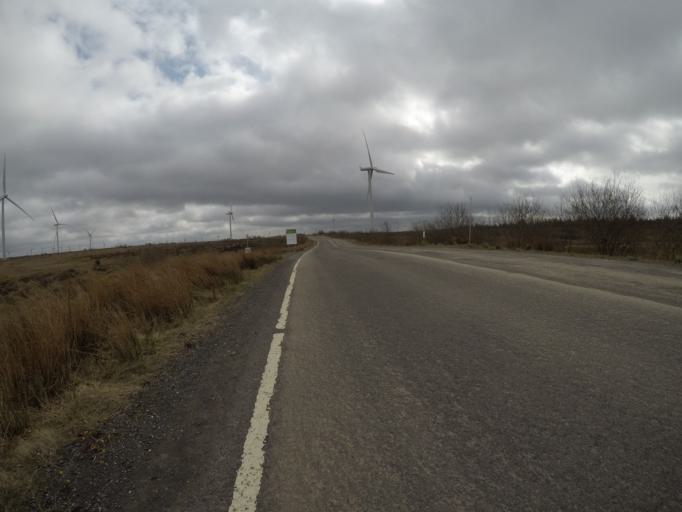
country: GB
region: Scotland
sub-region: East Renfrewshire
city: Newton Mearns
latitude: 55.7055
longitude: -4.3576
